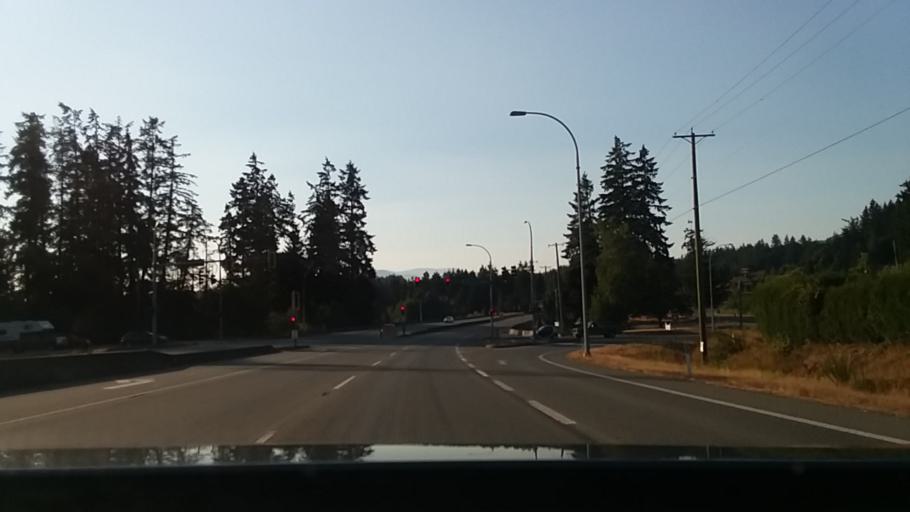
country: CA
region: British Columbia
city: Duncan
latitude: 48.7072
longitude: -123.6067
